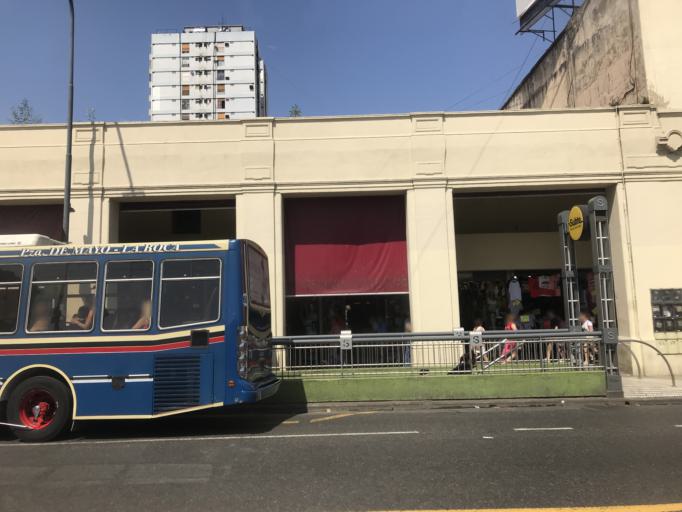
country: AR
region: Buenos Aires F.D.
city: Buenos Aires
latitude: -34.6092
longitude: -58.4060
